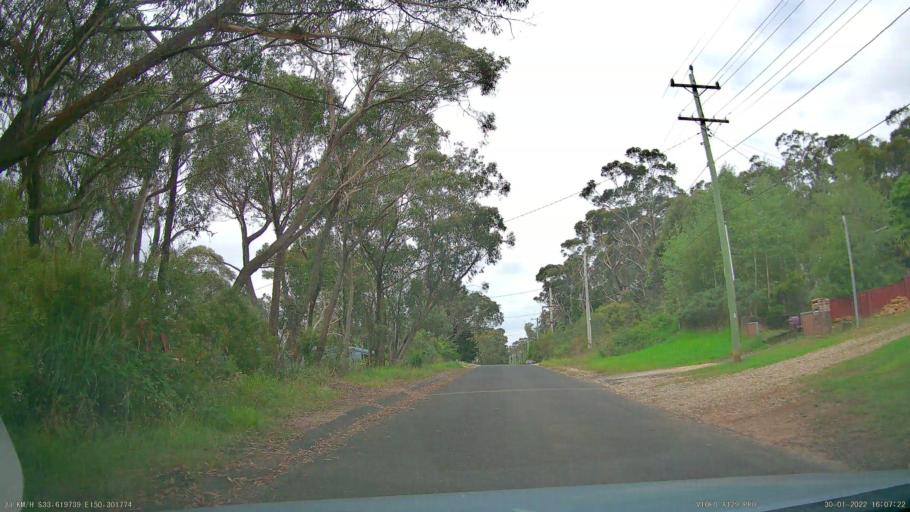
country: AU
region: New South Wales
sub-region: Blue Mountains Municipality
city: Blackheath
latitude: -33.6197
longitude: 150.3019
